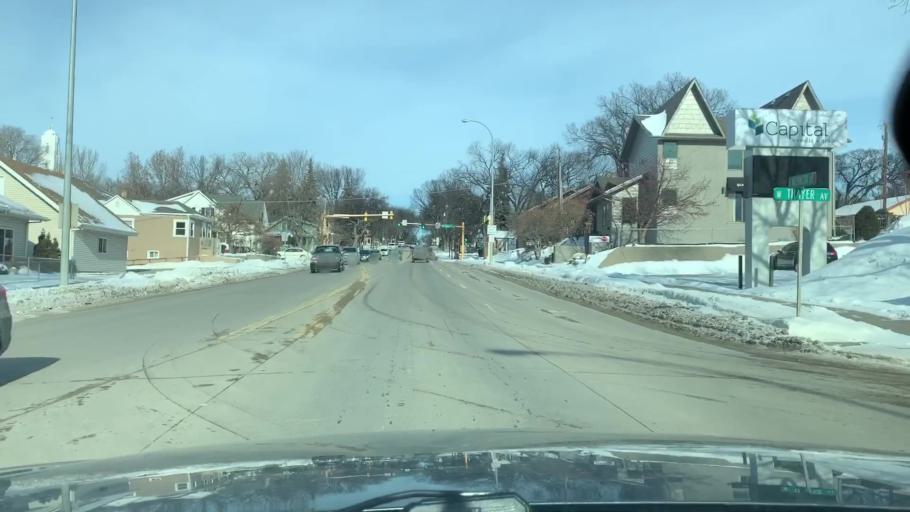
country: US
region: North Dakota
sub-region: Burleigh County
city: Bismarck
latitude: 46.8077
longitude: -100.7943
